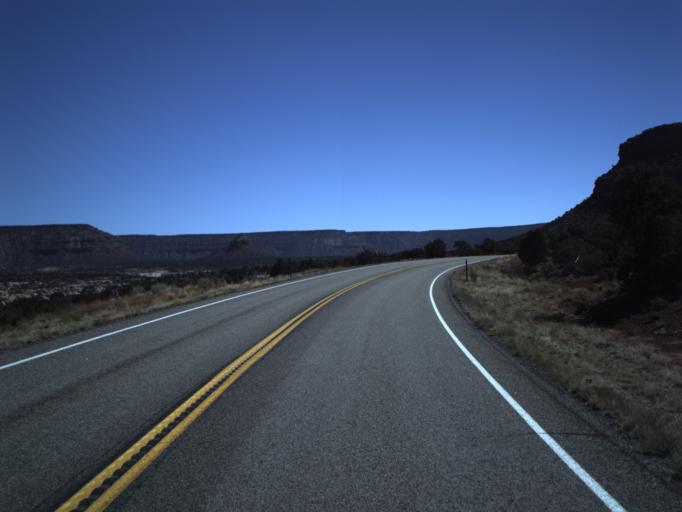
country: US
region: Utah
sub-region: San Juan County
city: Blanding
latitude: 37.6551
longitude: -110.1355
